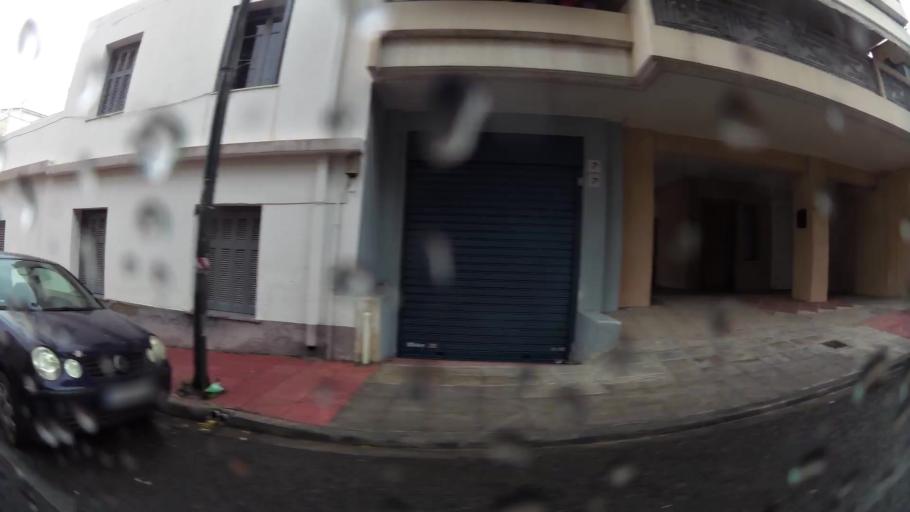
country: GR
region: Attica
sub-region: Nomarchia Athinas
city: Ymittos
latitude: 37.9540
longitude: 23.7544
